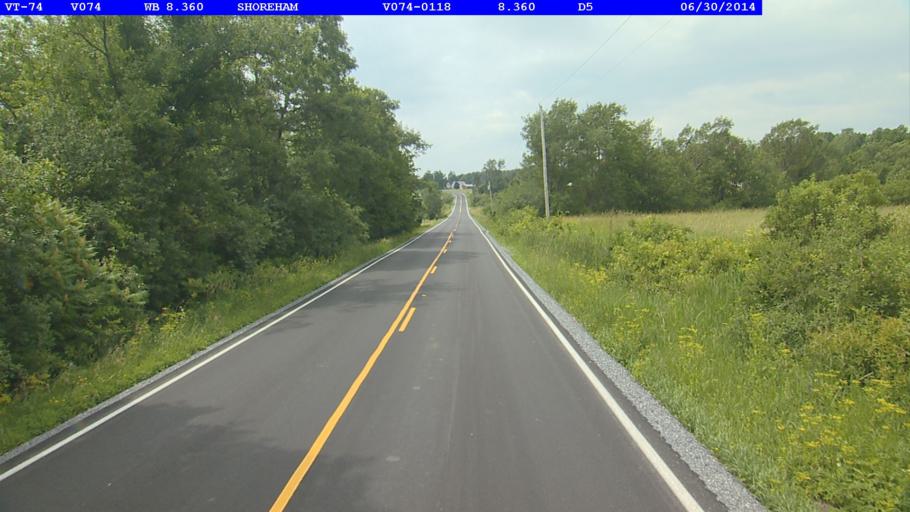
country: US
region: Vermont
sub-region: Addison County
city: Middlebury (village)
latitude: 43.9380
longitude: -73.2846
